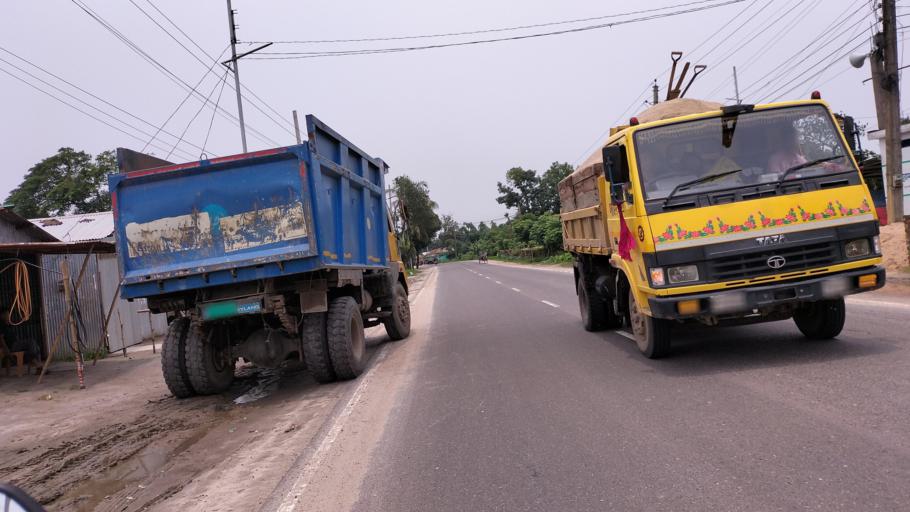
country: BD
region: Dhaka
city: Mymensingh
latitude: 24.7681
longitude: 90.4553
